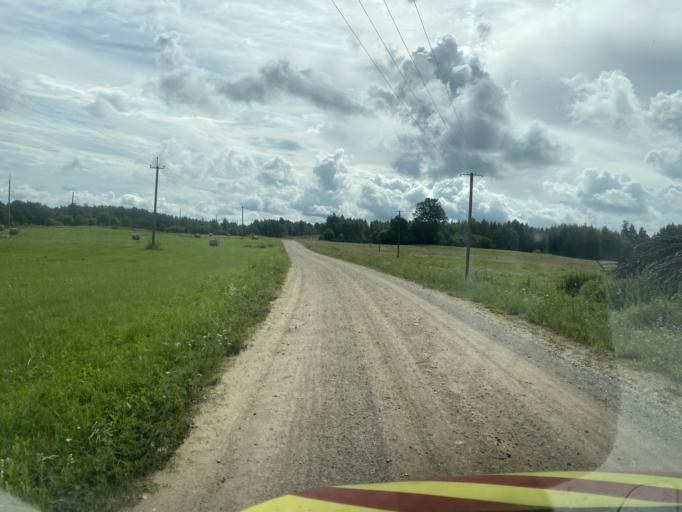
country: EE
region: Viljandimaa
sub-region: Karksi vald
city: Karksi-Nuia
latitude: 58.0877
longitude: 25.4907
